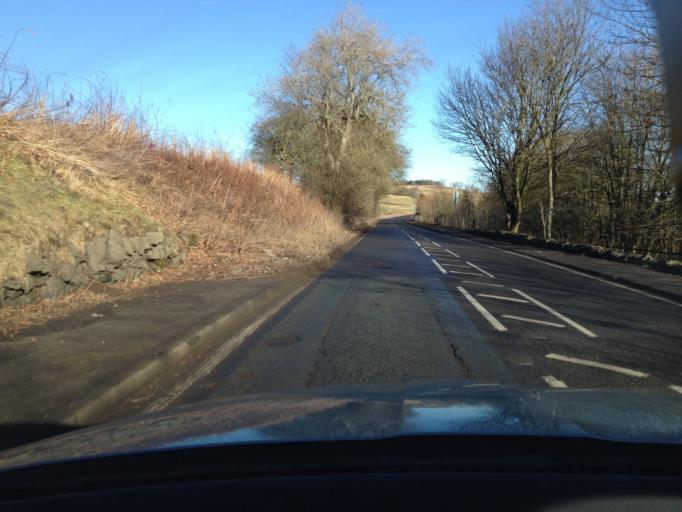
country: GB
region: Scotland
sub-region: Perth and Kinross
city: Milnathort
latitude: 56.2852
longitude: -3.3963
